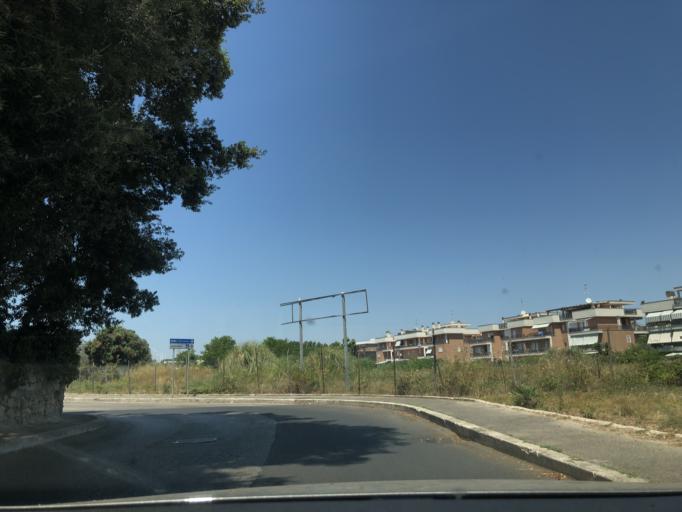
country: IT
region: Latium
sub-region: Citta metropolitana di Roma Capitale
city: Anzio
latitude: 41.4588
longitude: 12.6417
